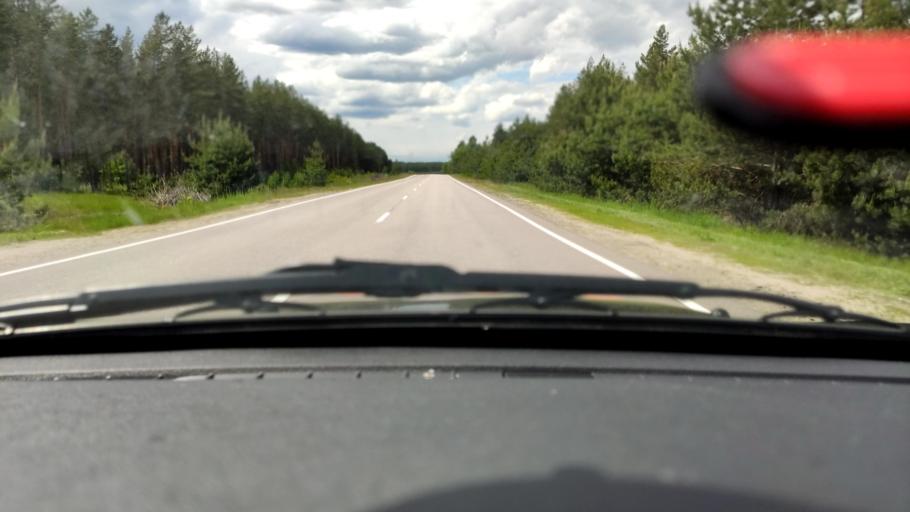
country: RU
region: Voronezj
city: Uryv-Pokrovka
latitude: 51.0526
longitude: 38.9670
